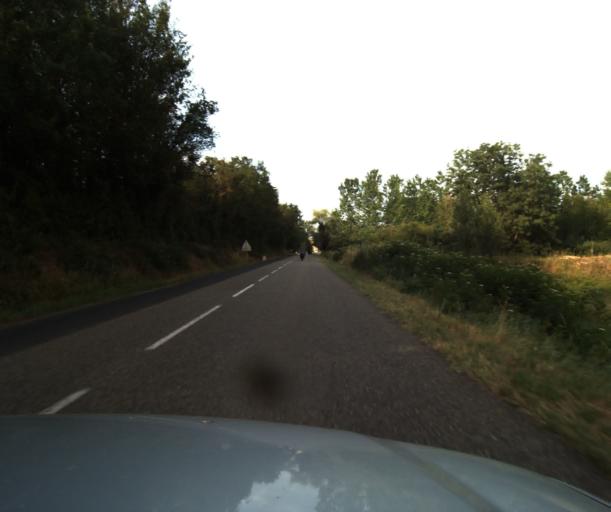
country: FR
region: Midi-Pyrenees
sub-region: Departement du Tarn-et-Garonne
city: Castelsarrasin
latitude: 43.9462
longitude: 1.0979
